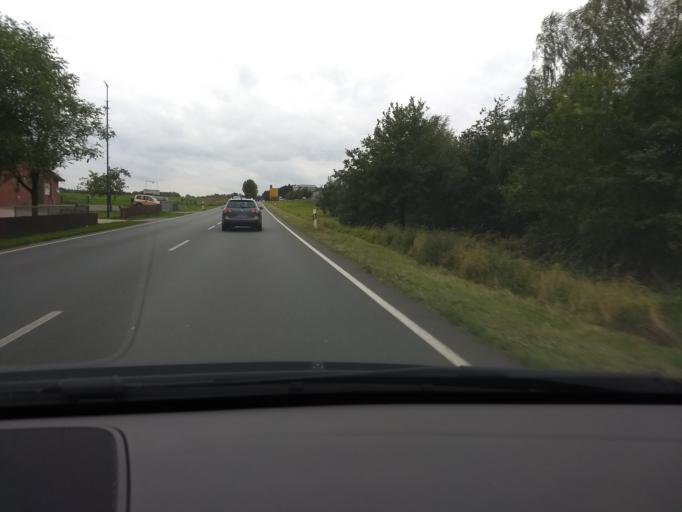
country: DE
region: North Rhine-Westphalia
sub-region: Regierungsbezirk Munster
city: Heiden
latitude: 51.8173
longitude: 6.9518
